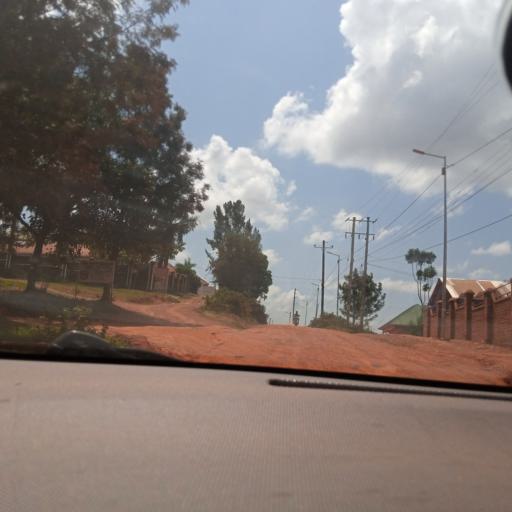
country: UG
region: Central Region
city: Masaka
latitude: -0.3281
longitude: 31.7393
